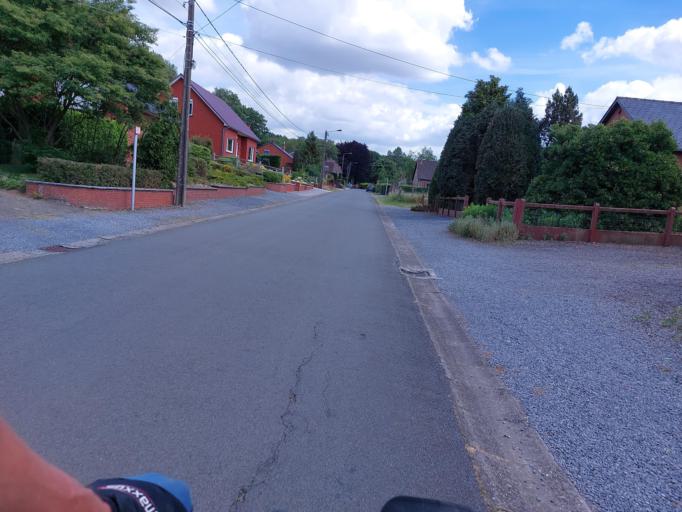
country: BE
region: Wallonia
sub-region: Province du Hainaut
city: Saint-Ghislain
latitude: 50.4920
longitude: 3.7989
